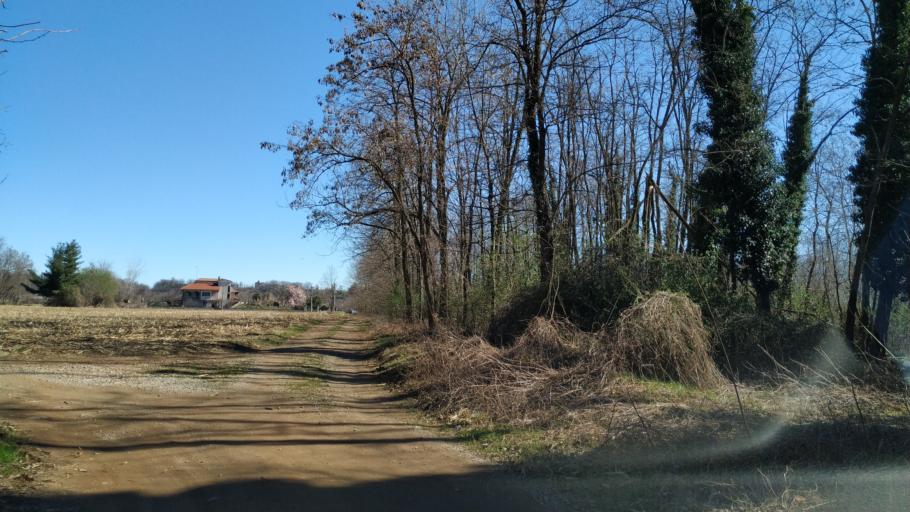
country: IT
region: Piedmont
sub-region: Provincia di Novara
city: Ghemme
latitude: 45.5970
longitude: 8.4056
